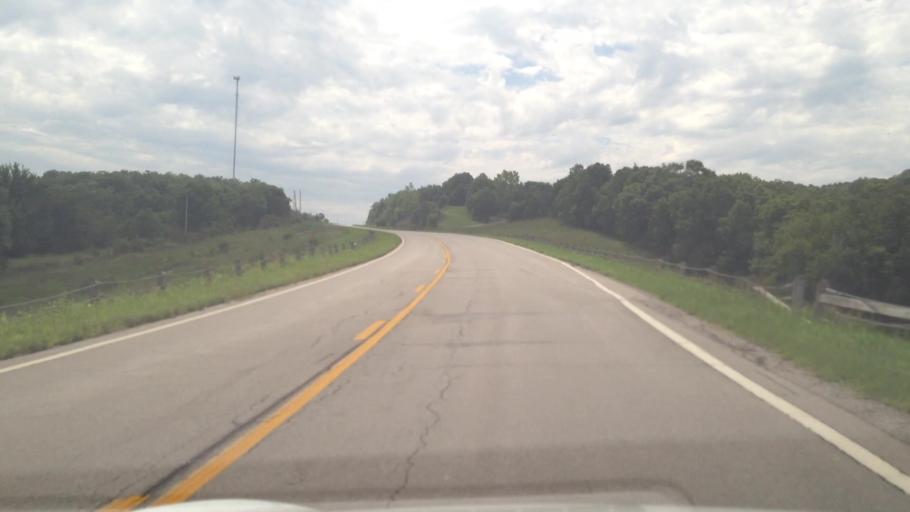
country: US
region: Kansas
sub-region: Bourbon County
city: Fort Scott
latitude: 37.8336
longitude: -94.9813
